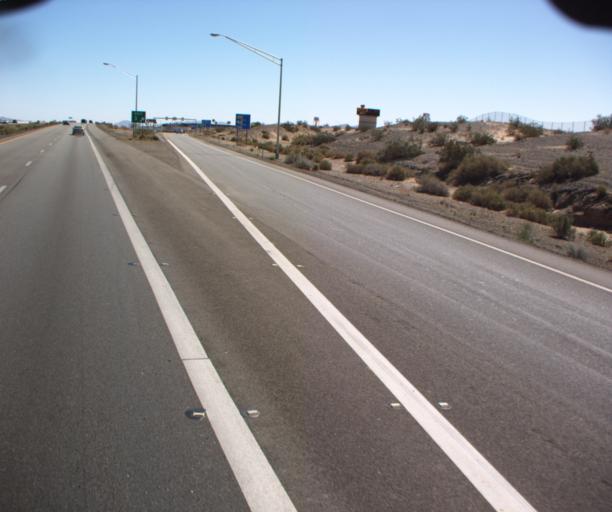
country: US
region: Arizona
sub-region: Yuma County
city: Yuma
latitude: 32.6898
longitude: -114.5862
